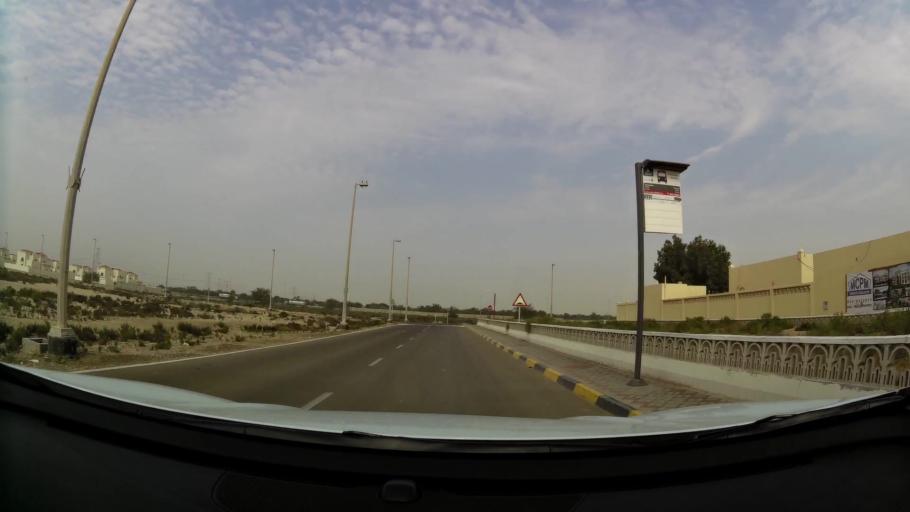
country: AE
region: Abu Dhabi
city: Abu Dhabi
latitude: 24.6739
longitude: 54.7518
